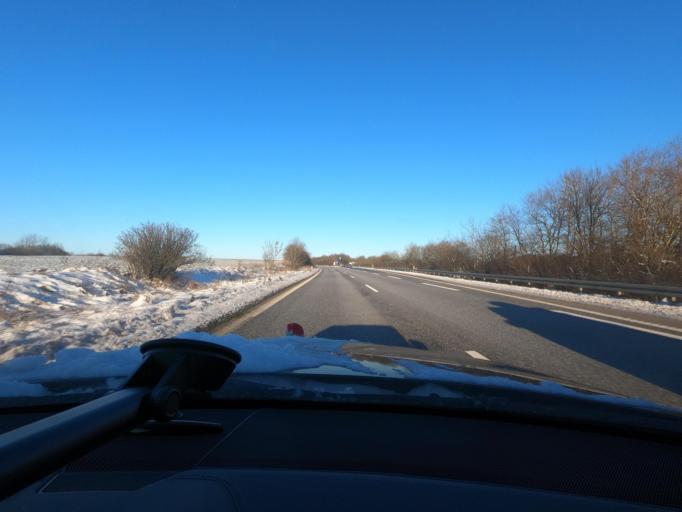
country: DK
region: South Denmark
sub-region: Aabenraa Kommune
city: Aabenraa
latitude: 55.0188
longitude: 9.3631
